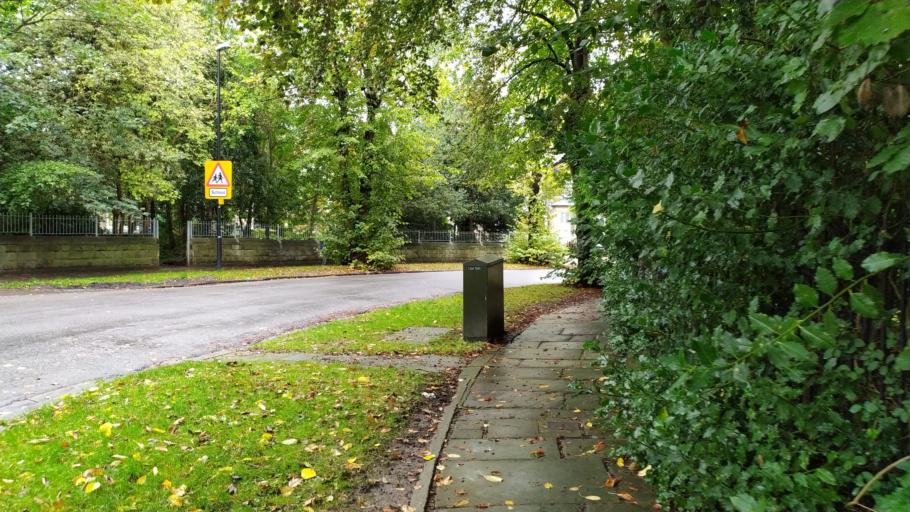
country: GB
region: England
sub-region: City and Borough of Leeds
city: Chapel Allerton
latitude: 53.8257
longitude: -1.5794
